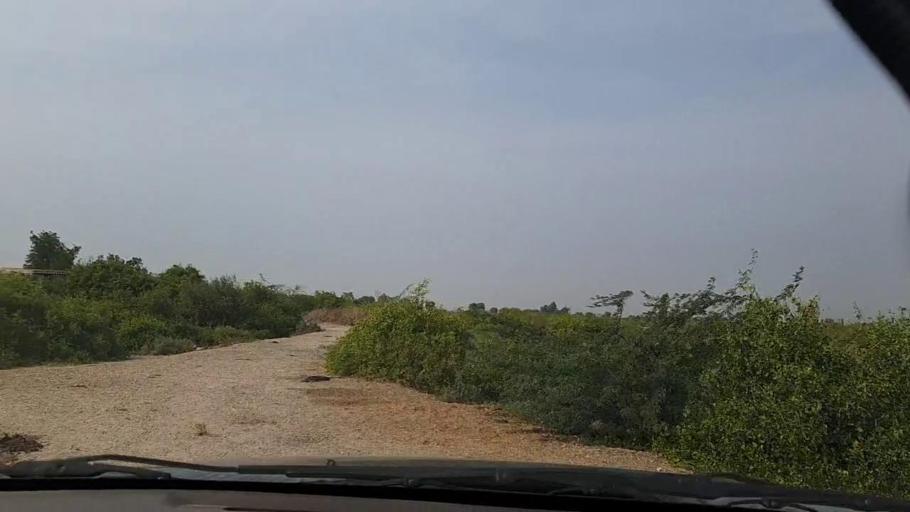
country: PK
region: Sindh
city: Thatta
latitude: 24.5795
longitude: 67.8492
